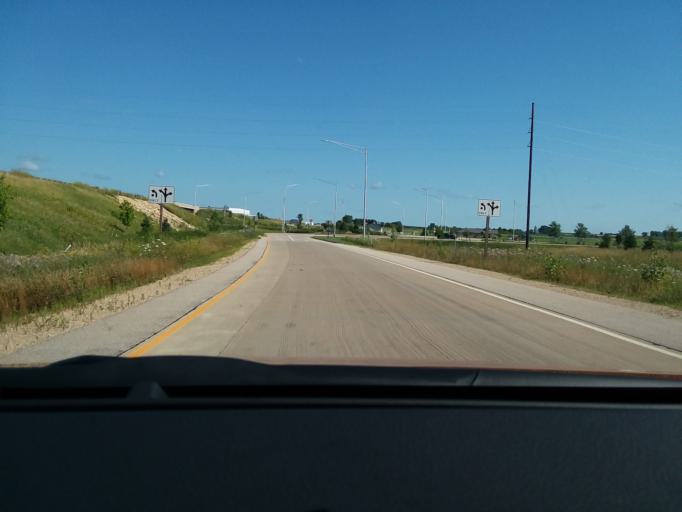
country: US
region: Wisconsin
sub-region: Dane County
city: De Forest
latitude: 43.2513
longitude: -89.3229
